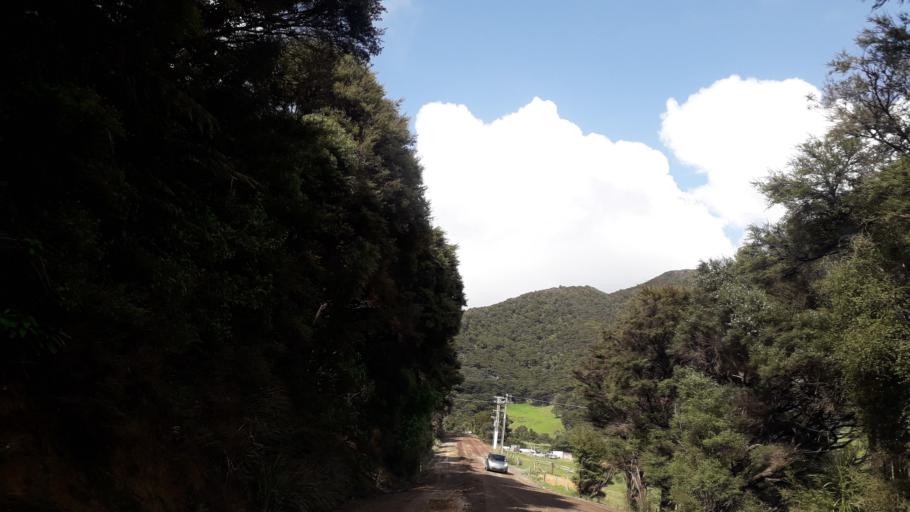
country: NZ
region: Northland
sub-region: Far North District
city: Paihia
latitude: -35.2611
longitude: 174.2644
